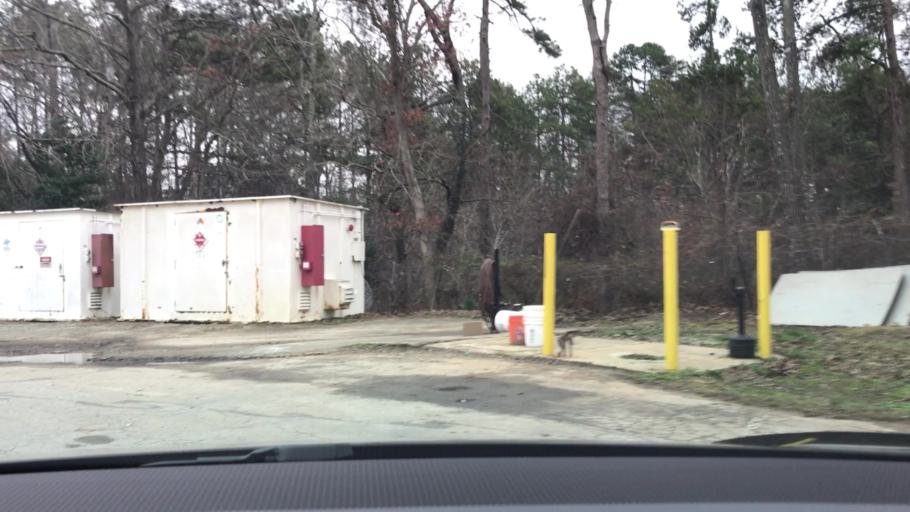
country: US
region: Georgia
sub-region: Gwinnett County
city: Buford
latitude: 34.1772
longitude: -84.0338
